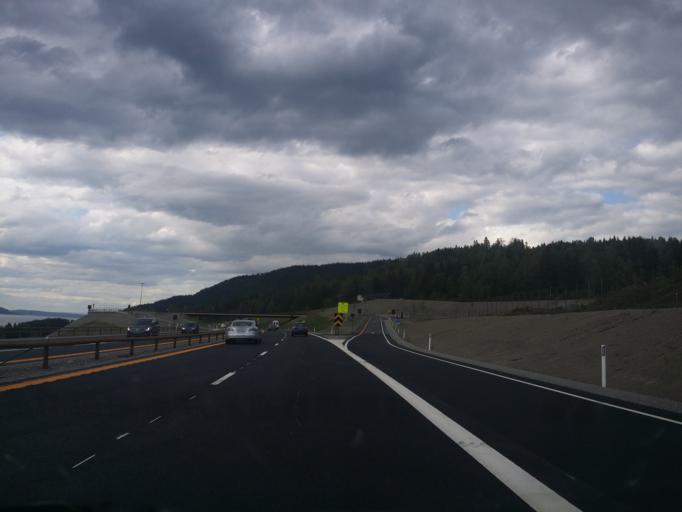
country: NO
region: Akershus
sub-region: Eidsvoll
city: Eidsvoll
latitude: 60.4109
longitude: 11.2404
